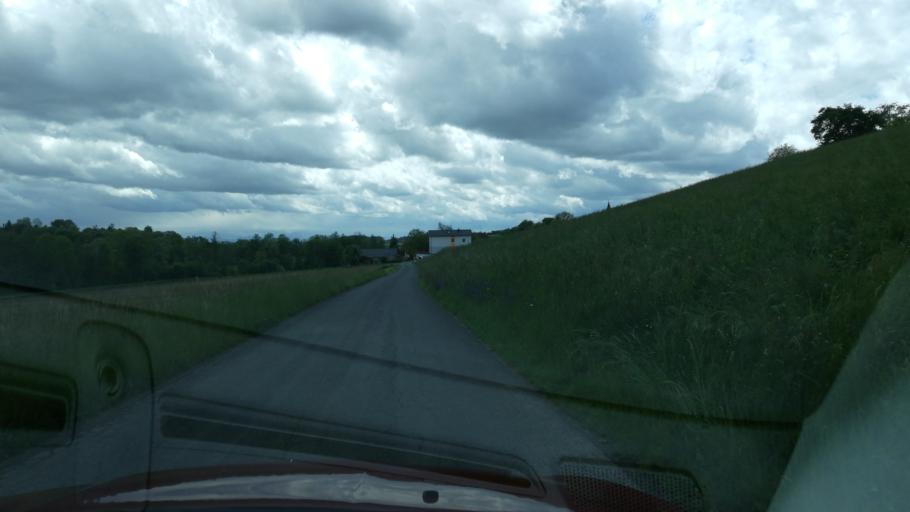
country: AT
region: Upper Austria
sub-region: Politischer Bezirk Linz-Land
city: Traun
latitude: 48.1841
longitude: 14.2072
